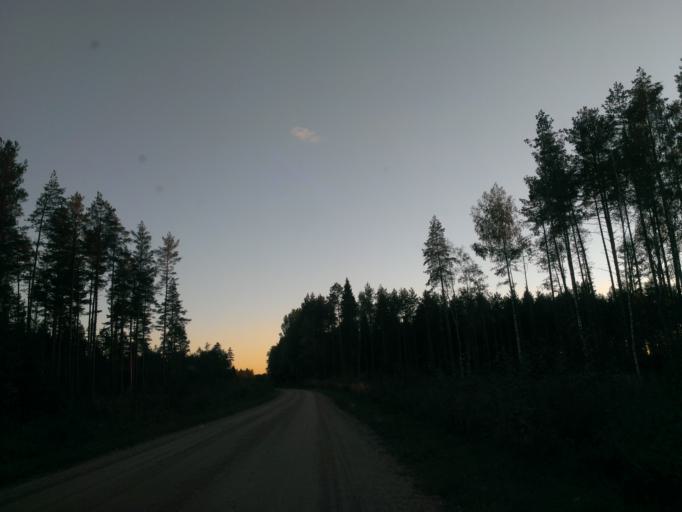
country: LV
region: Incukalns
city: Vangazi
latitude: 57.1119
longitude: 24.5664
